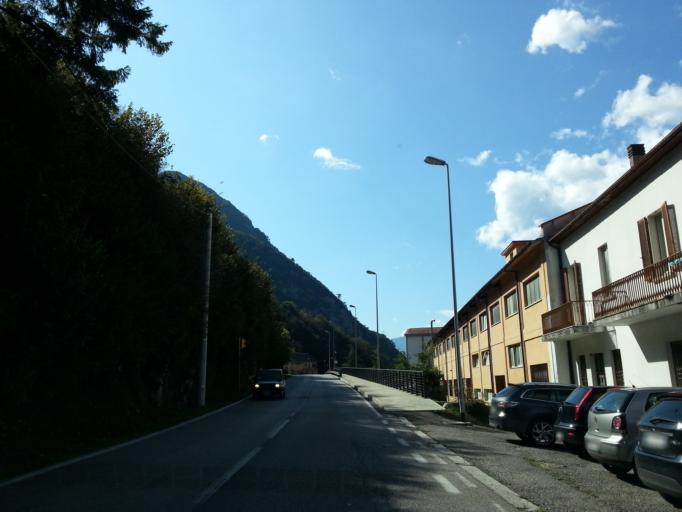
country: IT
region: Friuli Venezia Giulia
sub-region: Provincia di Udine
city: Moggio di Sotto
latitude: 46.4013
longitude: 13.1888
